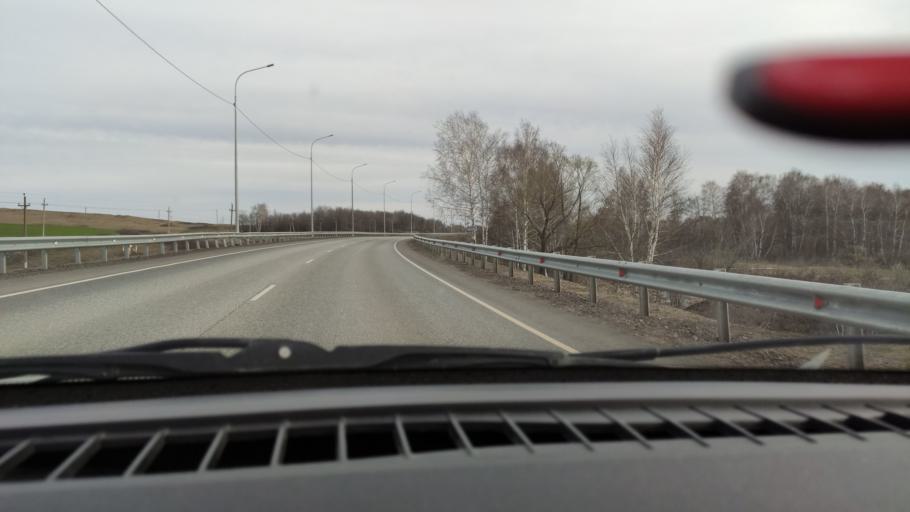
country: RU
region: Bashkortostan
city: Yermolayevo
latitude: 52.6501
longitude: 55.8387
